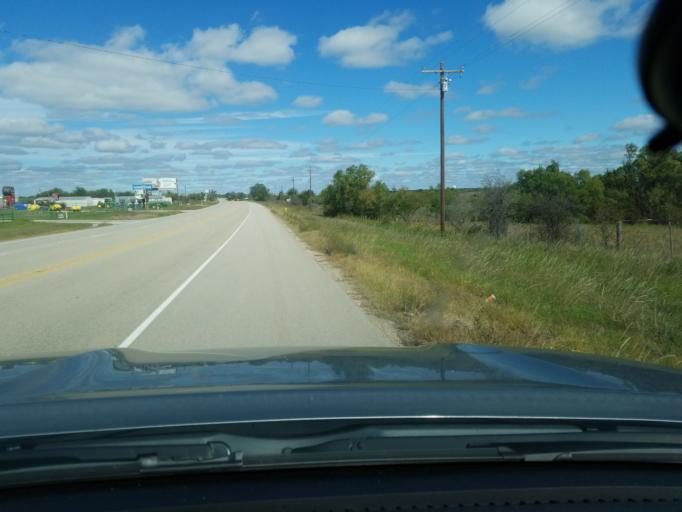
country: US
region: Texas
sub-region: Hamilton County
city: Hamilton
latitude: 31.6802
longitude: -98.1333
